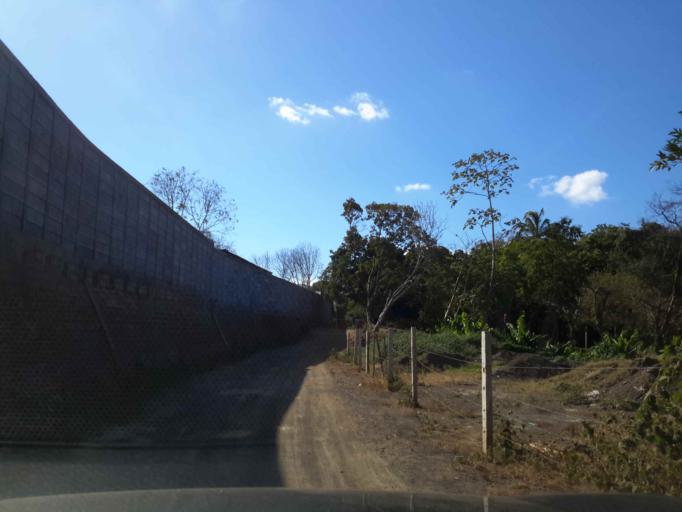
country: NI
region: Masaya
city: Ticuantepe
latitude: 12.0694
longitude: -86.2469
